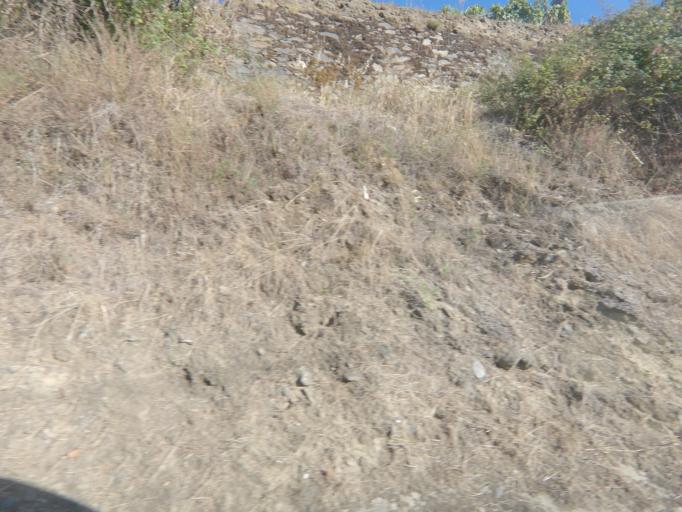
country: PT
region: Vila Real
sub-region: Peso da Regua
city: Peso da Regua
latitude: 41.1905
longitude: -7.7729
